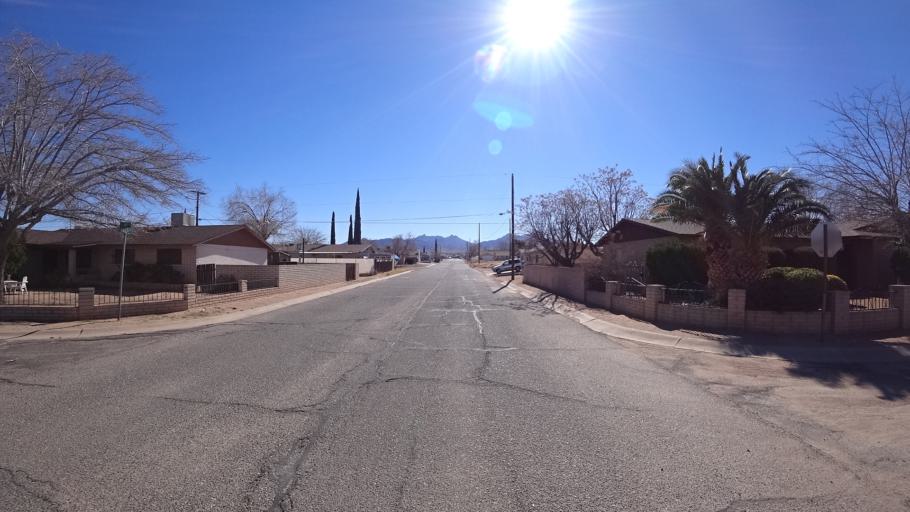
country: US
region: Arizona
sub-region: Mohave County
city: Kingman
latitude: 35.2084
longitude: -114.0238
